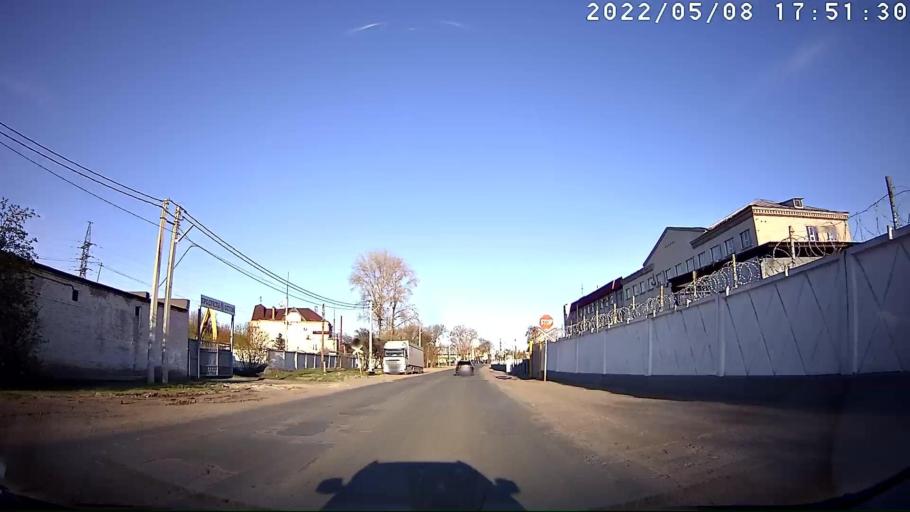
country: RU
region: Tatarstan
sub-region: Zelenodol'skiy Rayon
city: Zelenodolsk
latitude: 55.8412
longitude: 48.4948
